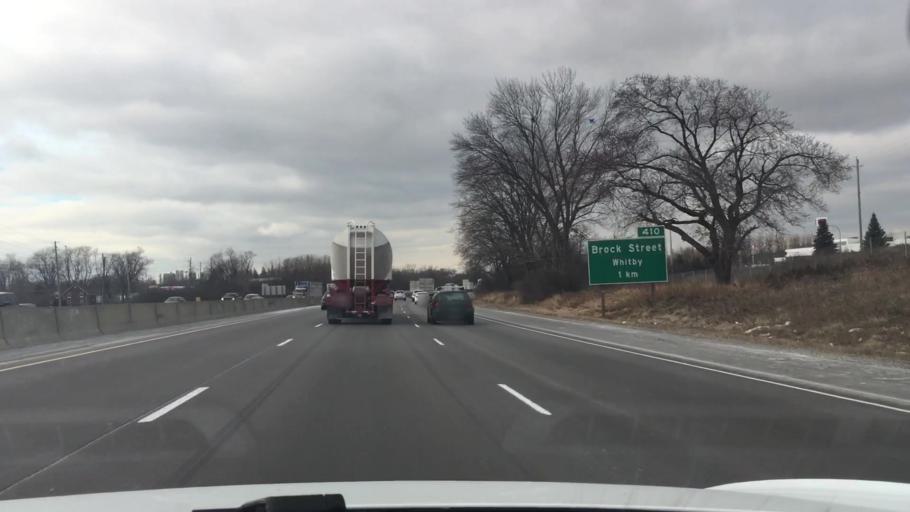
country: CA
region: Ontario
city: Oshawa
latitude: 43.8663
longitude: -78.9209
